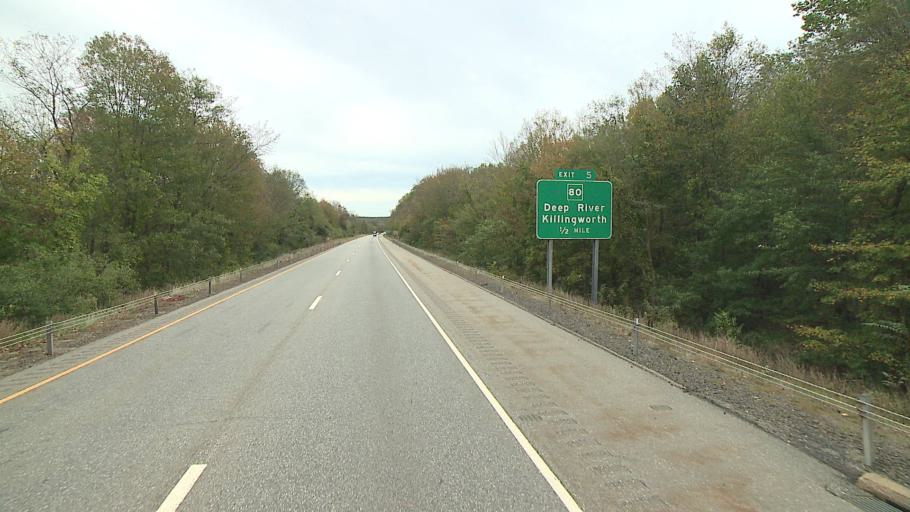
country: US
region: Connecticut
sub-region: Middlesex County
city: Chester Center
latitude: 41.3892
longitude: -72.4575
